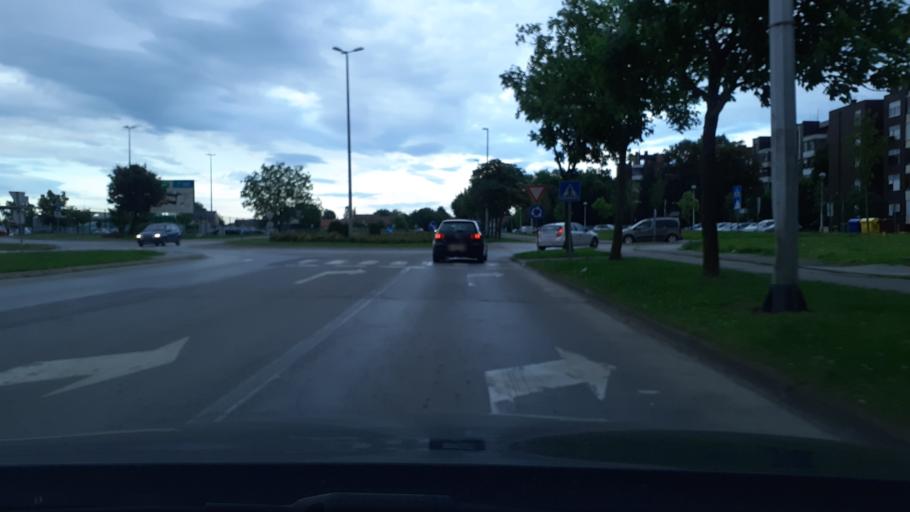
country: HR
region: Brodsko-Posavska
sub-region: Grad Slavonski Brod
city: Slavonski Brod
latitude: 45.1614
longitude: 18.0194
